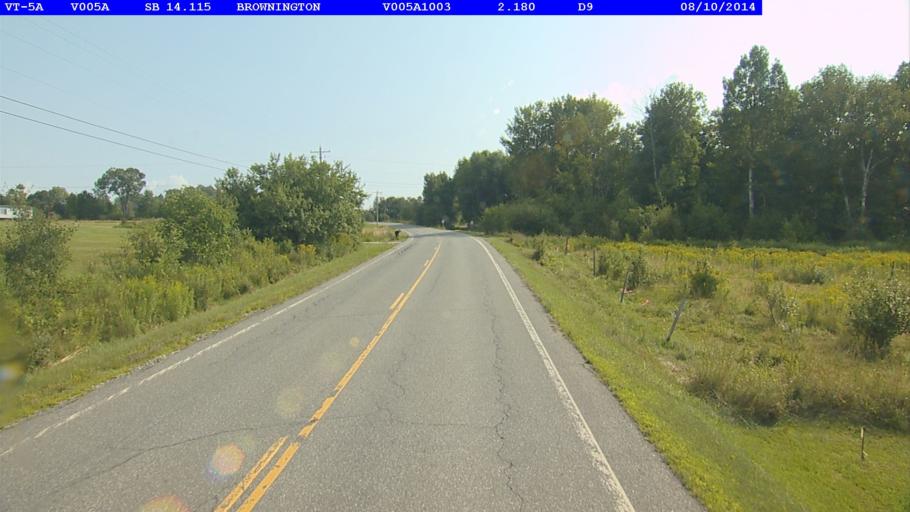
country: US
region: Vermont
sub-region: Orleans County
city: Newport
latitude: 44.8144
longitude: -72.0768
